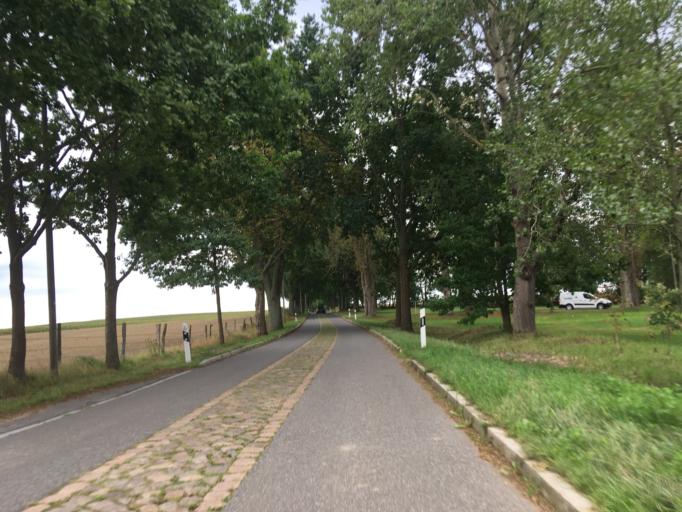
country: DE
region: Brandenburg
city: Friedrichswalde
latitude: 53.0338
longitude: 13.6845
